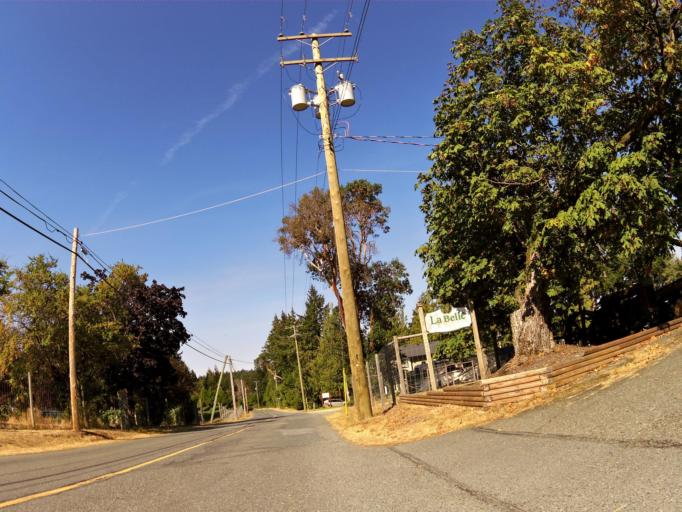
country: CA
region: British Columbia
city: North Saanich
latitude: 48.6767
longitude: -123.5511
